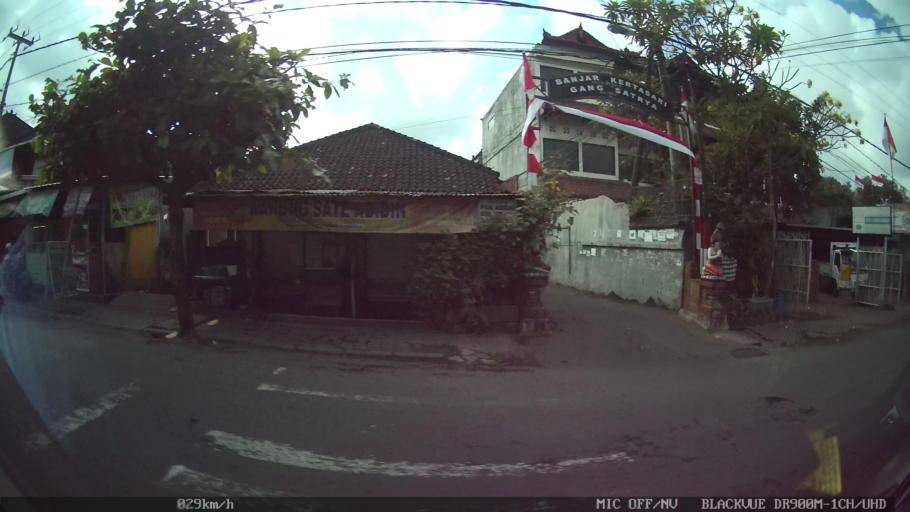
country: ID
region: Bali
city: Banjar Kertasari
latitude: -8.6258
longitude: 115.2081
